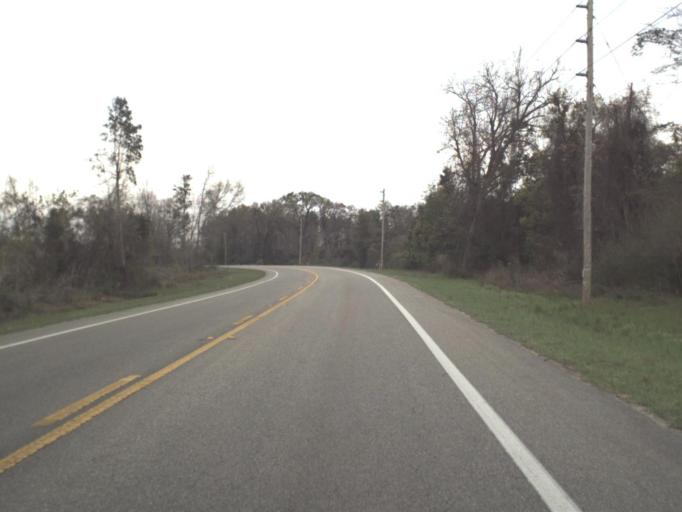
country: US
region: Florida
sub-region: Gulf County
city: Wewahitchka
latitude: 30.1639
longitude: -85.2088
